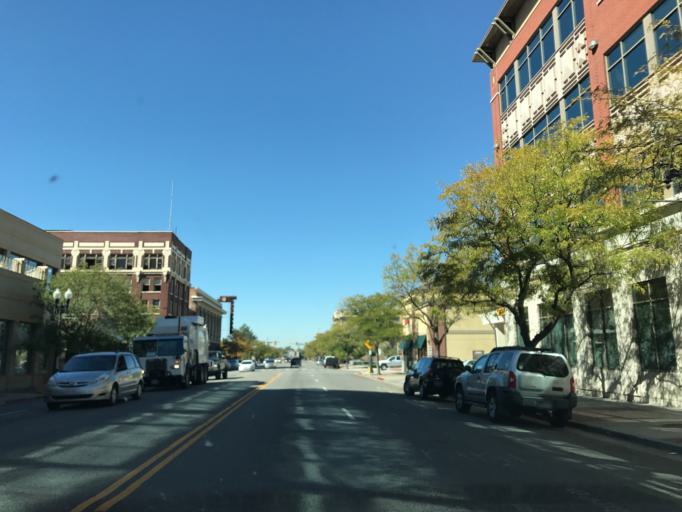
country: US
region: Utah
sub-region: Weber County
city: Ogden
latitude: 41.2228
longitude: -111.9710
